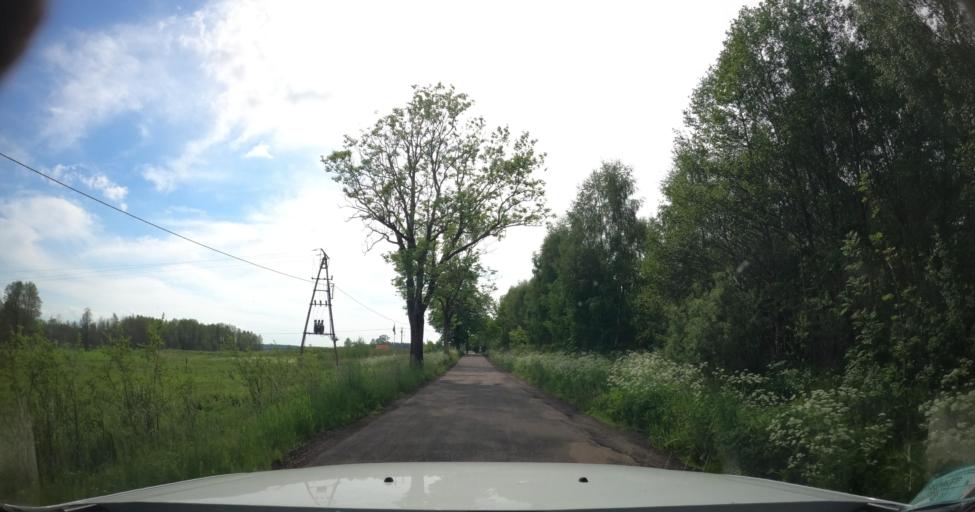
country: PL
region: Warmian-Masurian Voivodeship
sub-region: Powiat lidzbarski
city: Lidzbark Warminski
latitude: 54.1120
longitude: 20.4801
